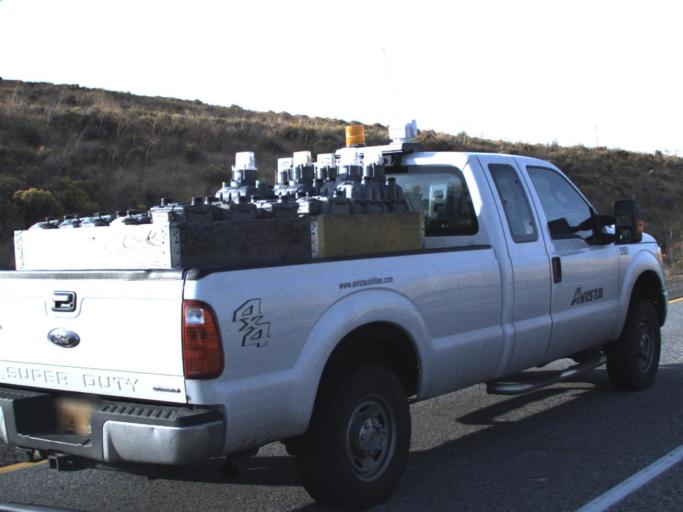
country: US
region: Washington
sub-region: Benton County
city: Highland
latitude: 46.1197
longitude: -119.2021
